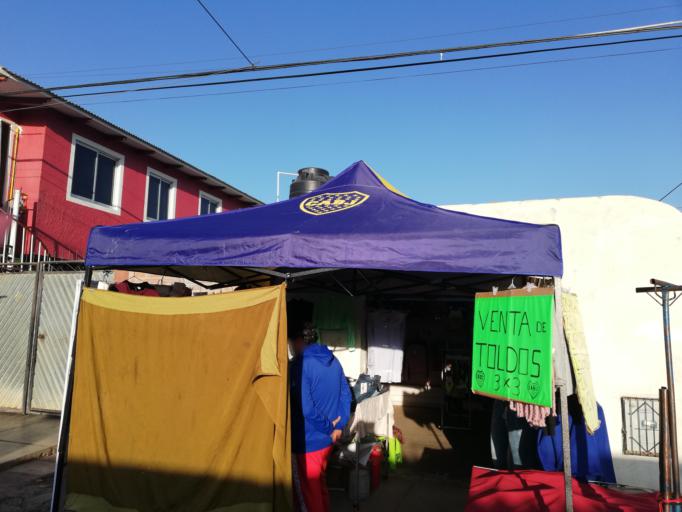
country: BO
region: Cochabamba
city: Cochabamba
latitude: -17.3621
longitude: -66.1840
